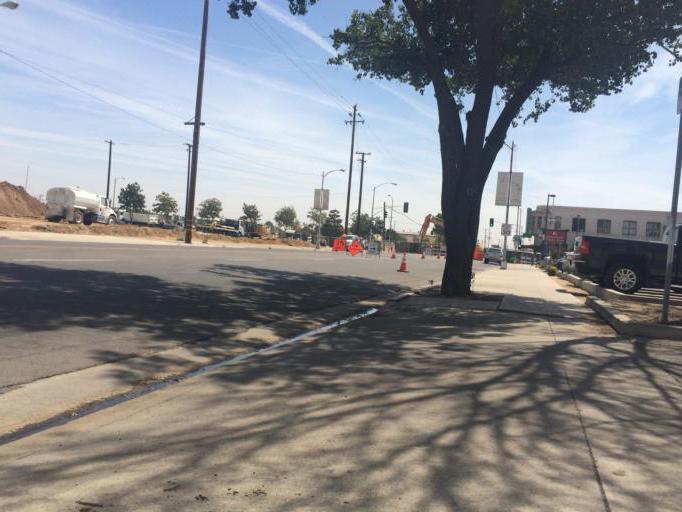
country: US
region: California
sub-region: Fresno County
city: Fresno
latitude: 36.7308
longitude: -119.7937
